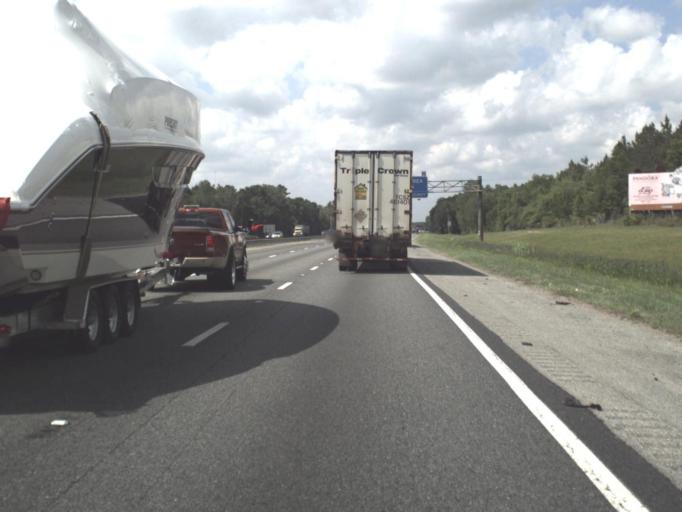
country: US
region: Florida
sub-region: Saint Johns County
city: Fruit Cove
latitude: 30.0739
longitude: -81.4986
